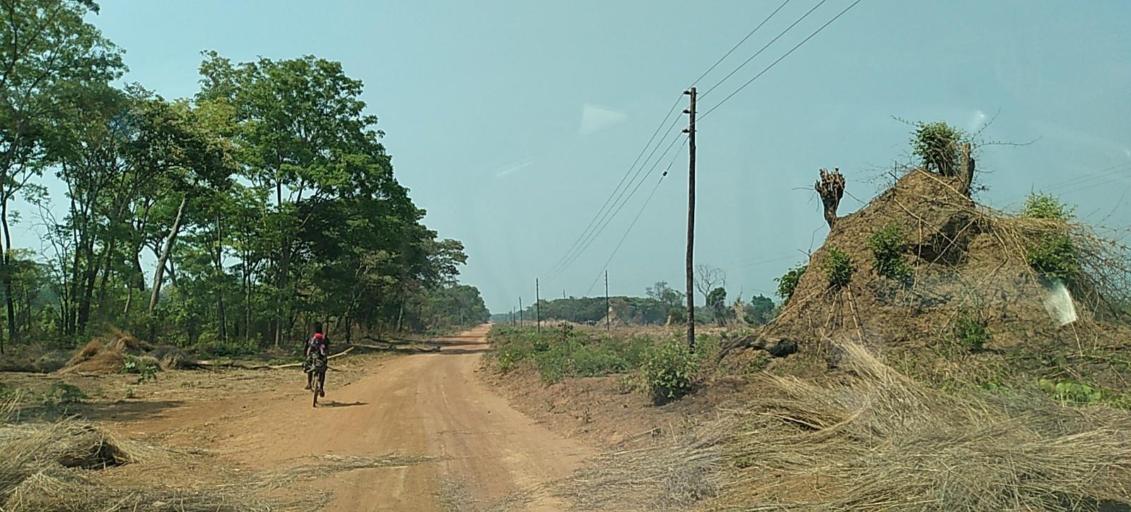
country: ZM
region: Copperbelt
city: Kalulushi
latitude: -13.0902
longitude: 27.4078
